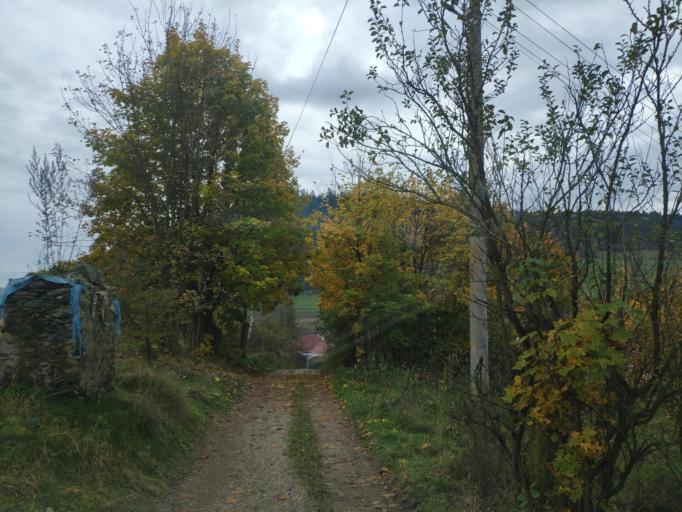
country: SK
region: Kosicky
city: Spisska Nova Ves
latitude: 48.8392
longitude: 20.6170
